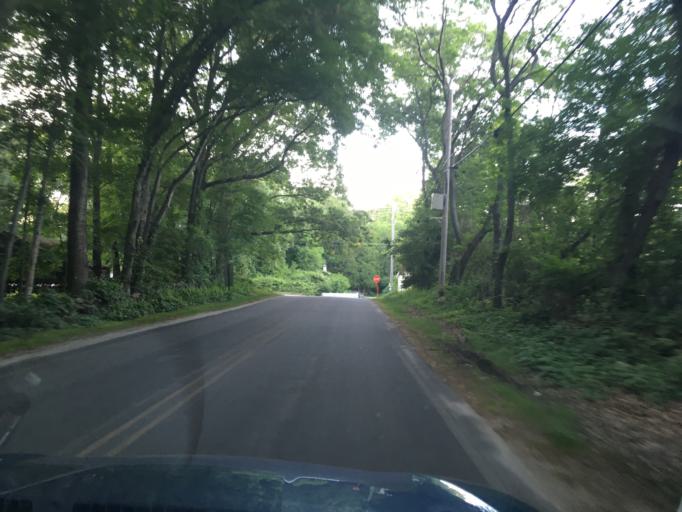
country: US
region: Rhode Island
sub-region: Kent County
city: West Warwick
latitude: 41.6422
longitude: -71.5145
